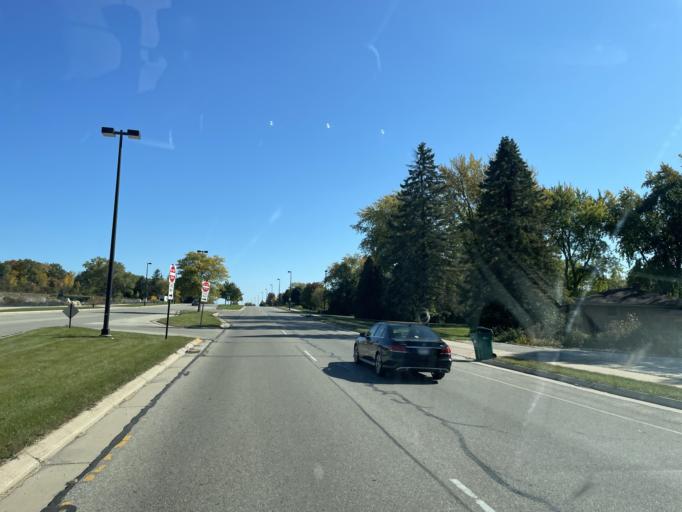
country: US
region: Wisconsin
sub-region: Waukesha County
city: Butler
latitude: 43.1477
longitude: -88.0734
